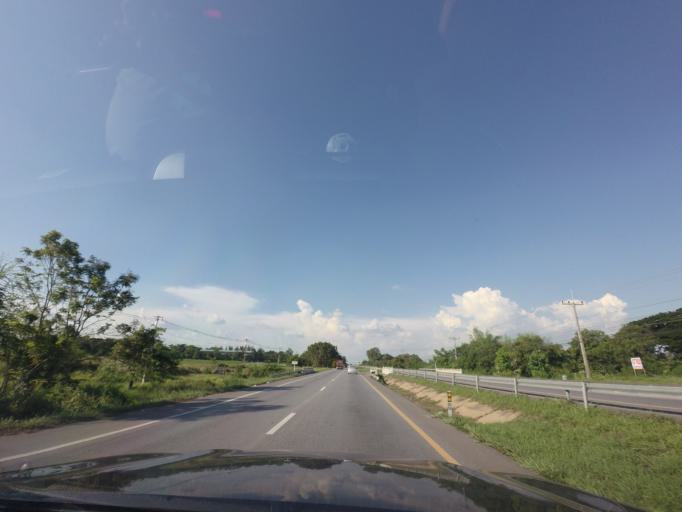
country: TH
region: Khon Kaen
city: Non Sila
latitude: 15.9722
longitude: 102.6932
